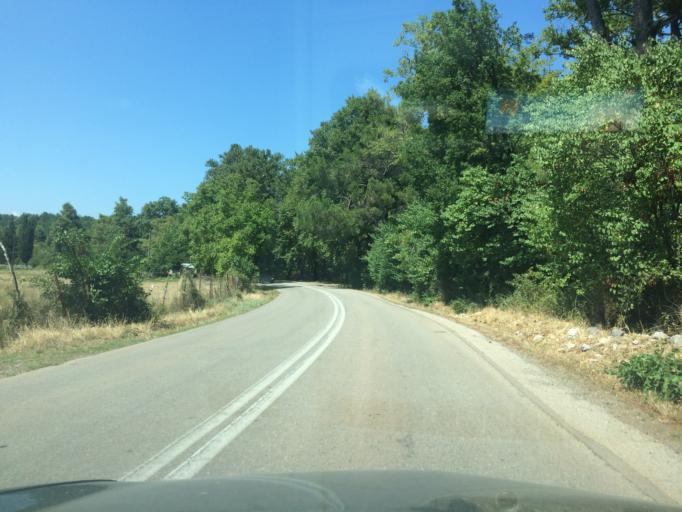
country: GR
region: Central Greece
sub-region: Nomos Evvoias
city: Prokopion
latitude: 38.7183
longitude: 23.5172
